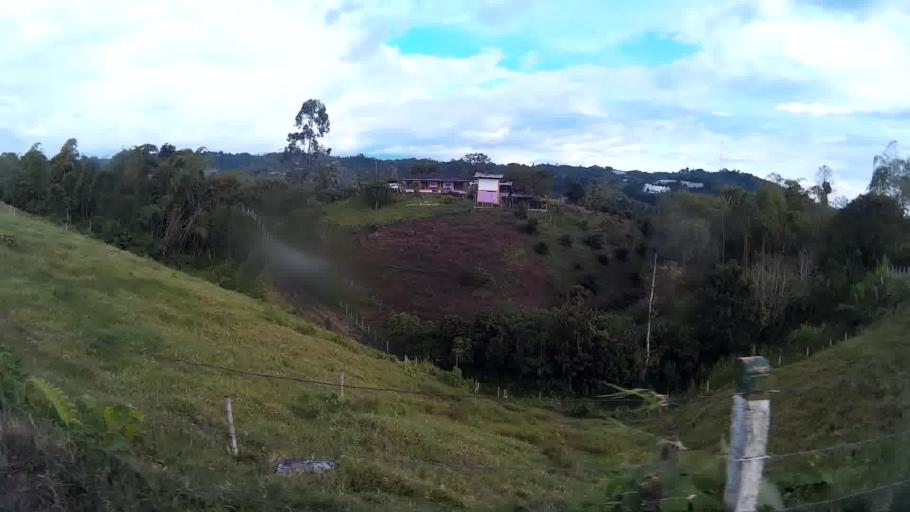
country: CO
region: Valle del Cauca
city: Ulloa
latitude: 4.7241
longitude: -75.7011
